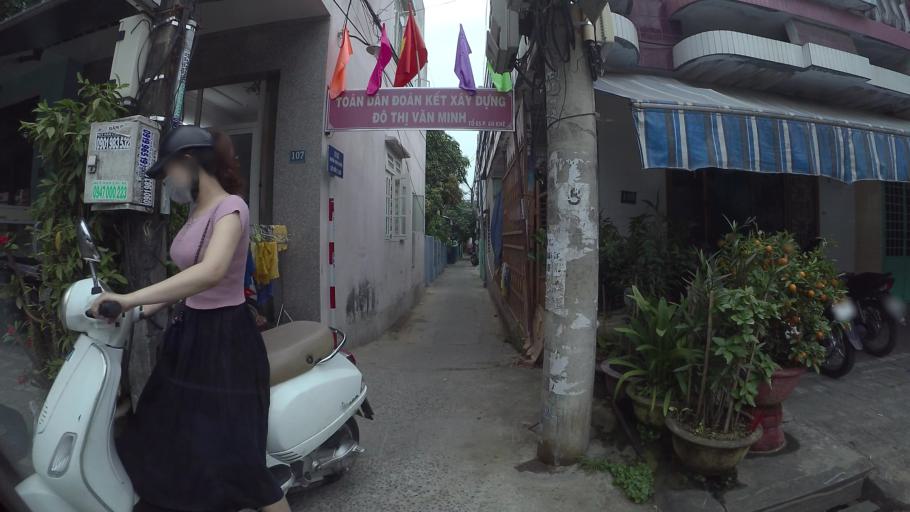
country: VN
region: Da Nang
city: Thanh Khe
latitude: 16.0593
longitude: 108.1807
